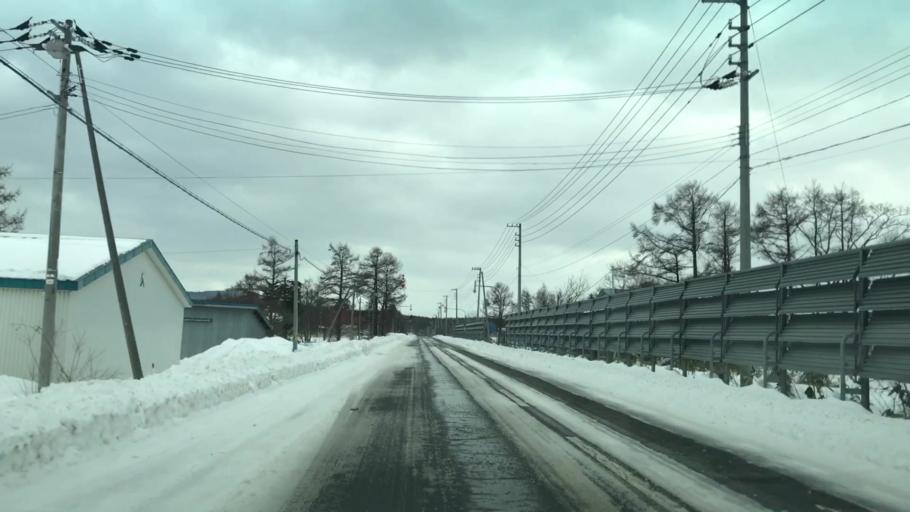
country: JP
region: Hokkaido
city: Yoichi
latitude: 43.3101
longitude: 140.5498
